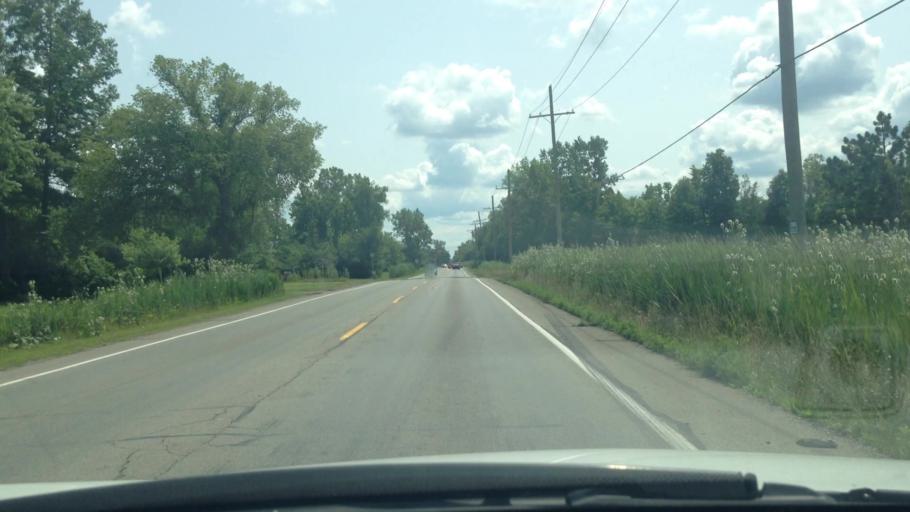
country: US
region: Michigan
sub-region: Wayne County
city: Taylor
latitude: 42.2138
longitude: -83.3072
